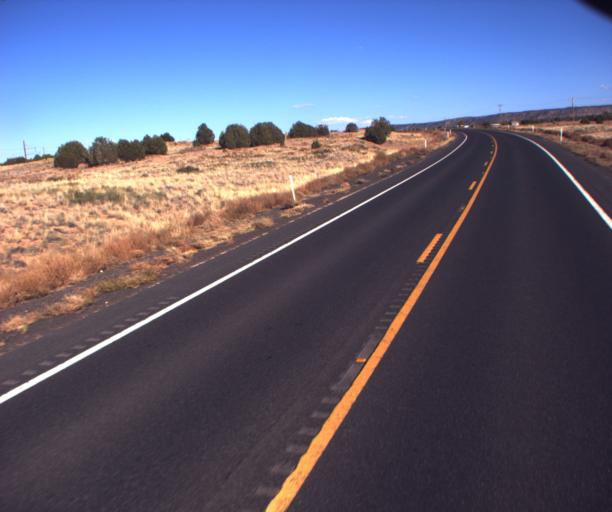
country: US
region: Arizona
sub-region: Coconino County
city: Kaibito
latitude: 36.4408
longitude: -110.7426
